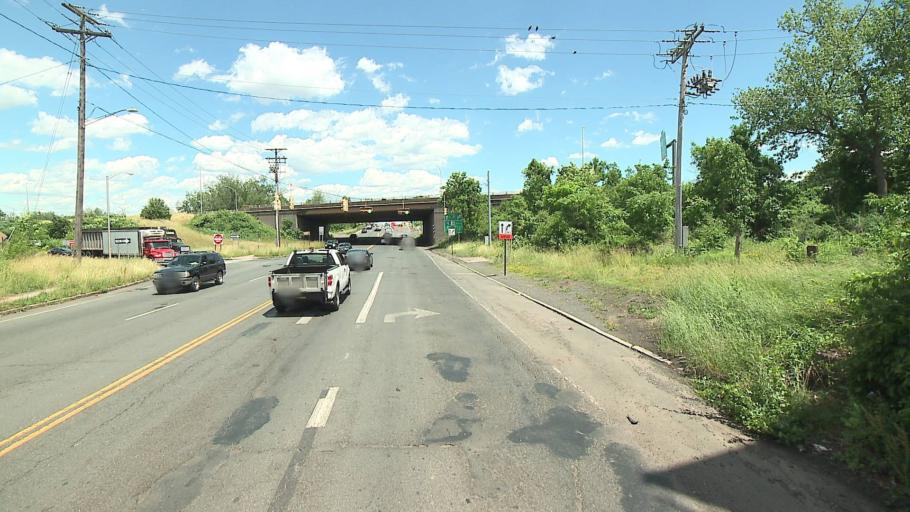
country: US
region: Connecticut
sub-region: Hartford County
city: Wethersfield
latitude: 41.7384
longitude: -72.6656
